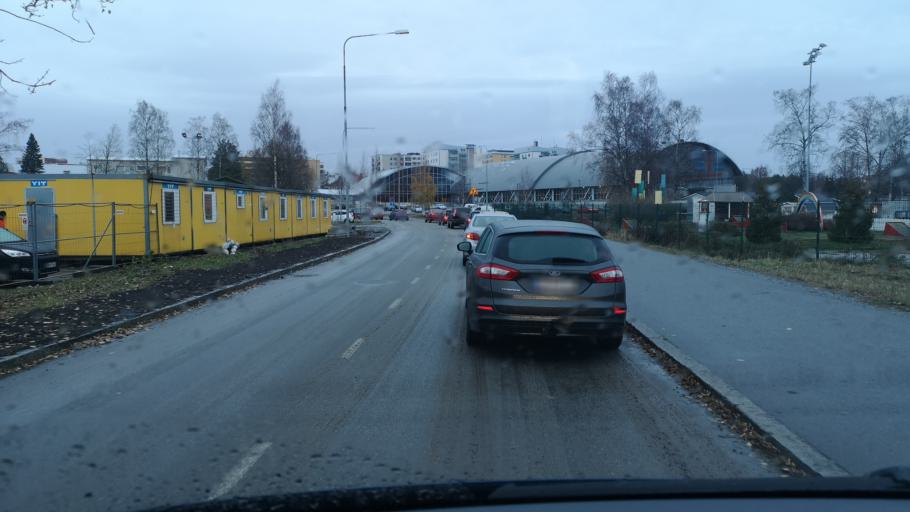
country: FI
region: Ostrobothnia
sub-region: Vaasa
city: Vaasa
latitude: 63.0847
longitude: 21.6201
